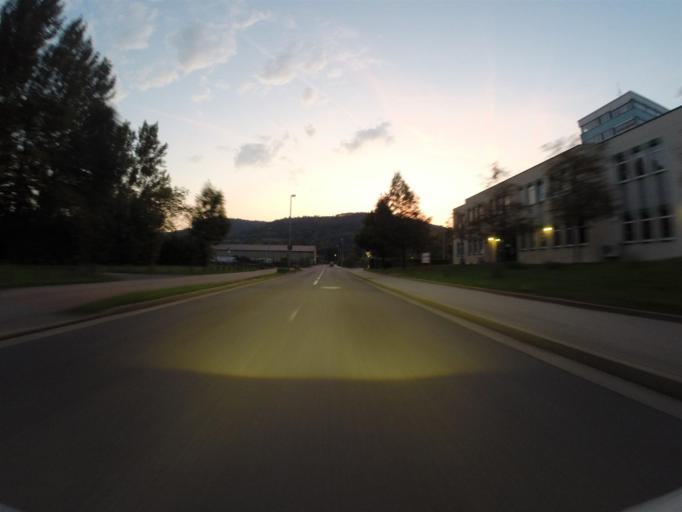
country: DE
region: Thuringia
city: Sulza
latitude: 50.8835
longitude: 11.5975
